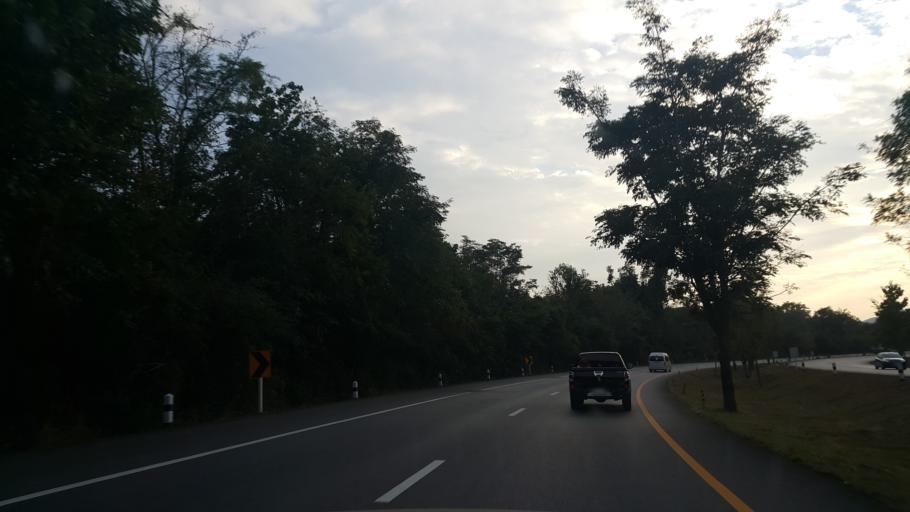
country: TH
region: Lampang
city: Sop Prap
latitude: 17.8182
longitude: 99.2827
